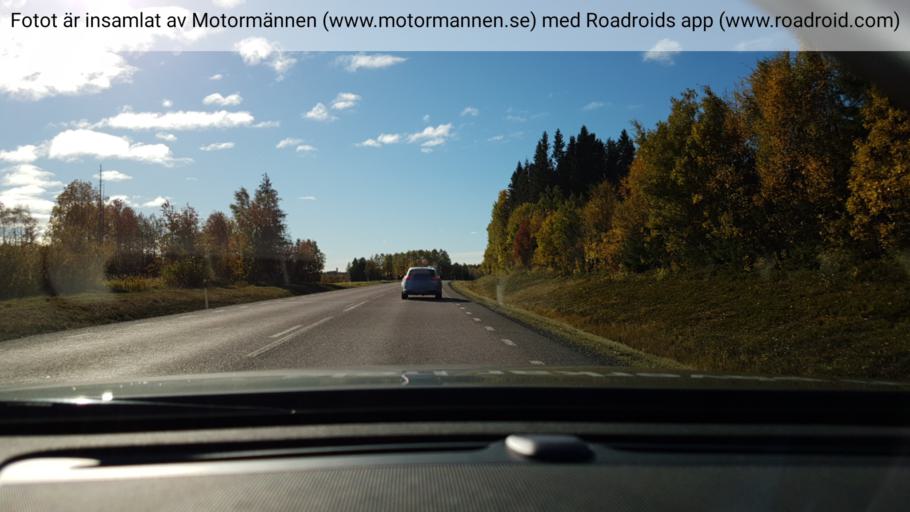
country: SE
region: Vaesterbotten
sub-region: Skelleftea Kommun
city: Burea
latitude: 64.4007
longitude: 21.3011
